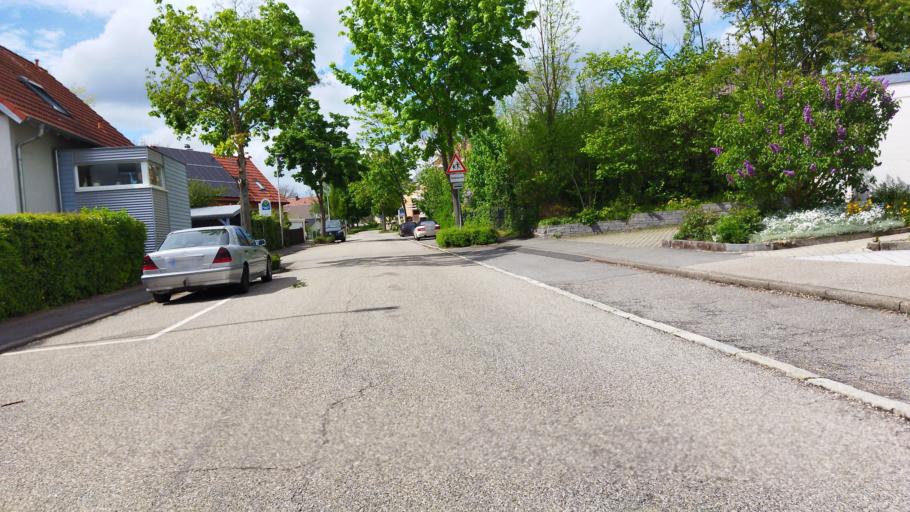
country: DE
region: Baden-Wuerttemberg
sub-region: Regierungsbezirk Stuttgart
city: Bad Rappenau
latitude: 49.2126
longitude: 9.0979
